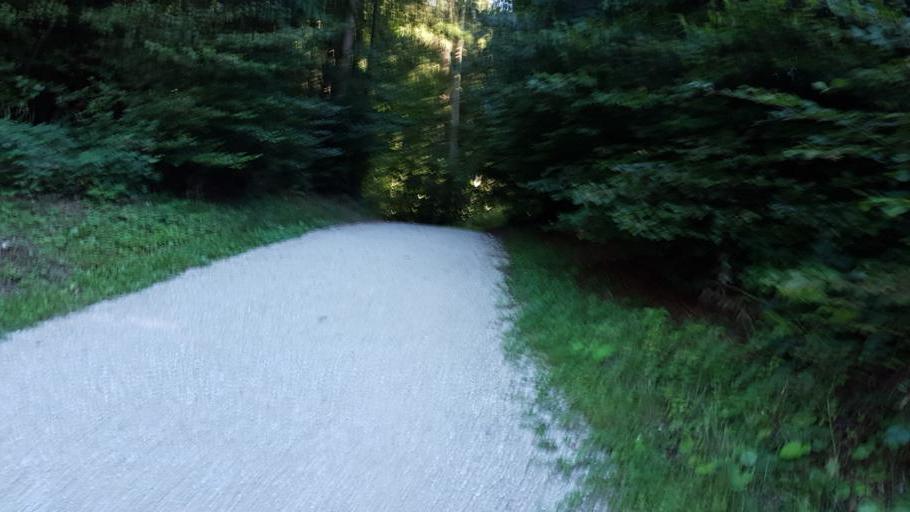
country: CH
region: Bern
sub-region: Bern-Mittelland District
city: Muri
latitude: 46.9439
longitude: 7.5035
